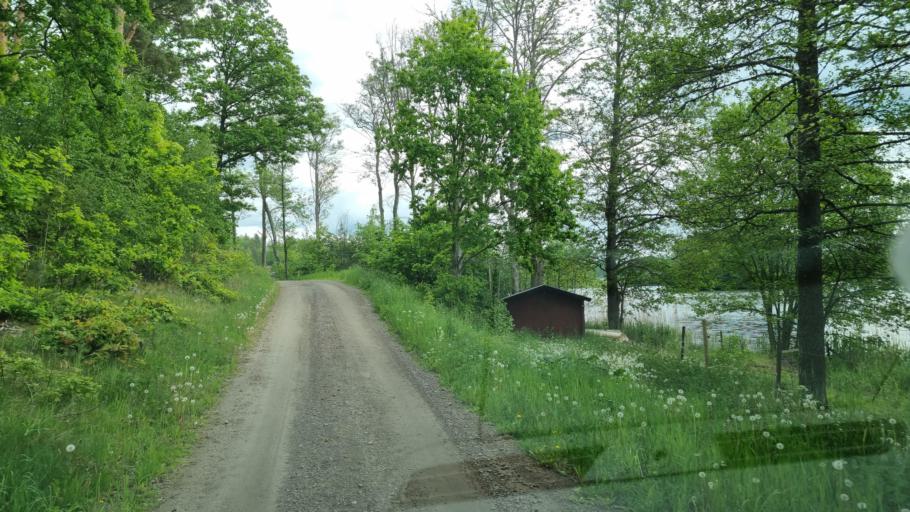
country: SE
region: OEstergoetland
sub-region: Atvidabergs Kommun
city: Atvidaberg
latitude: 58.1899
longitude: 16.0475
